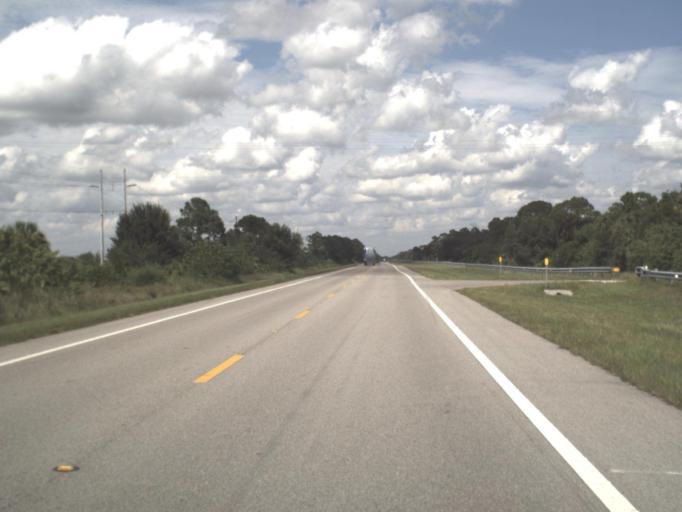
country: US
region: Florida
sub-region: Collier County
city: Immokalee
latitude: 26.3245
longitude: -81.3431
